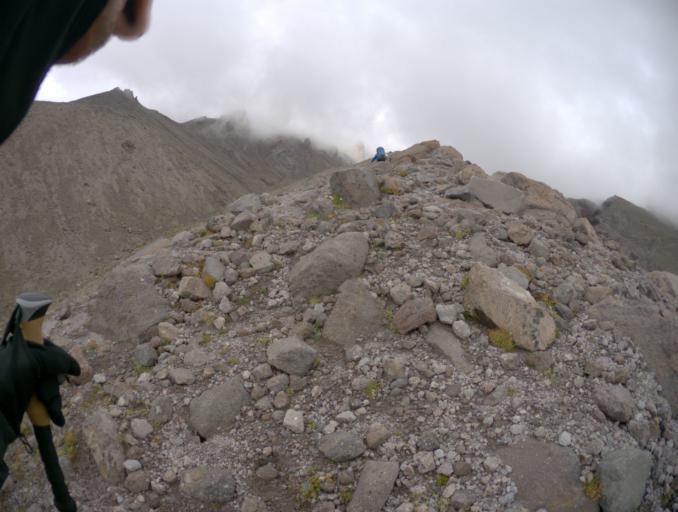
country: RU
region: Kabardino-Balkariya
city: Terskol
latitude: 43.3821
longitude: 42.3834
